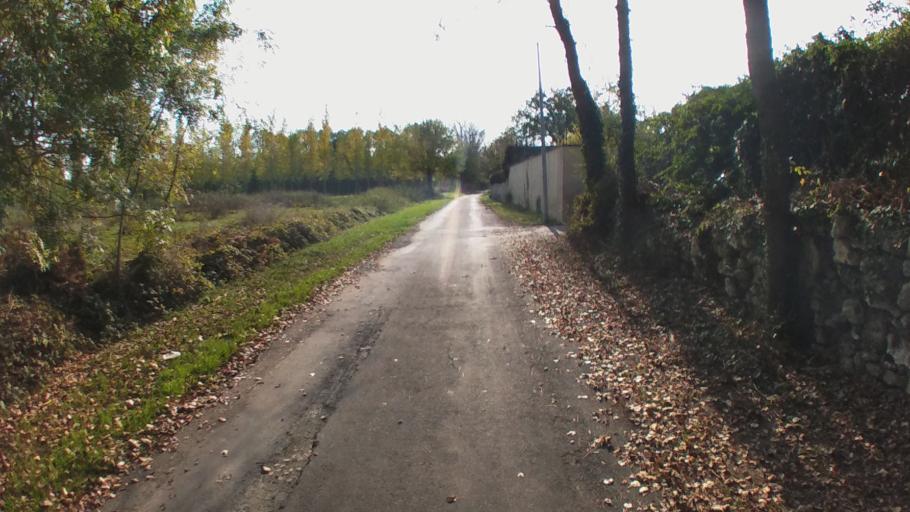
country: FR
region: Pays de la Loire
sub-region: Departement de Maine-et-Loire
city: Chace
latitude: 47.1986
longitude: -0.0925
